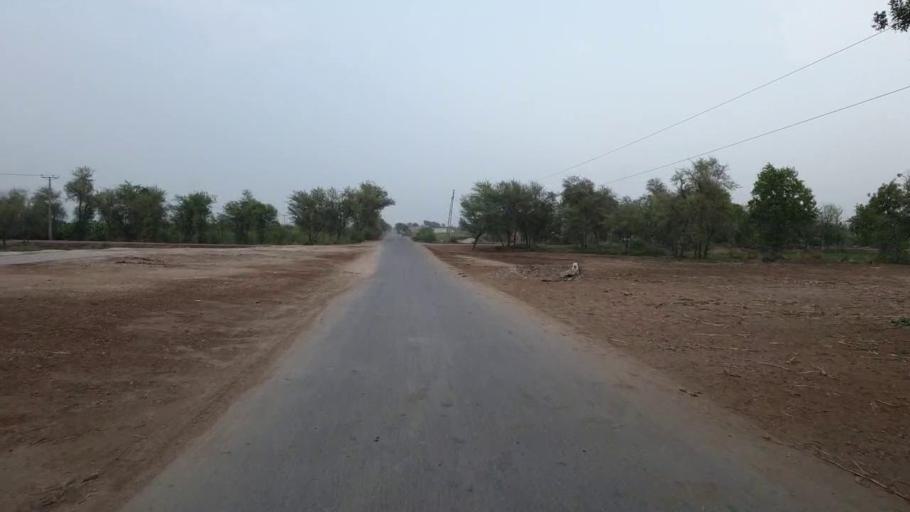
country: PK
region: Sindh
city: Daur
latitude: 26.4108
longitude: 68.2360
